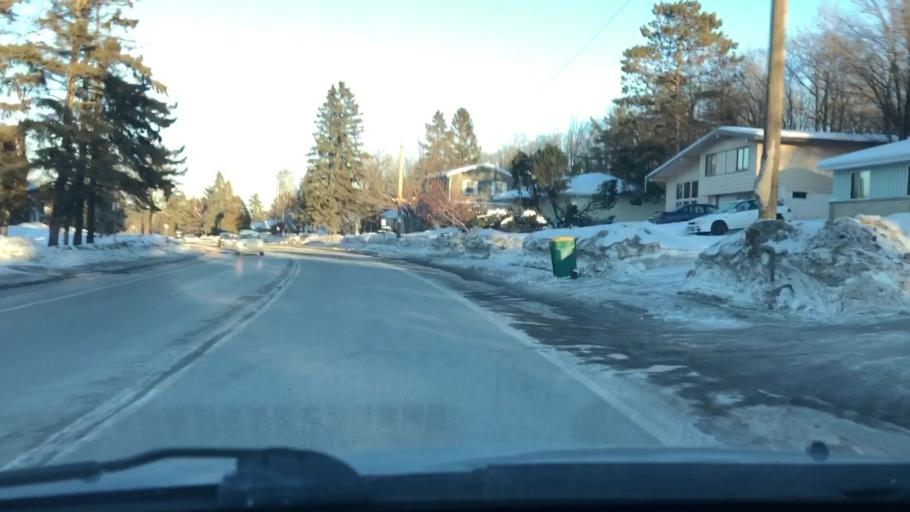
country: US
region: Minnesota
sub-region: Saint Louis County
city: Duluth
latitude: 46.8225
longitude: -92.0959
